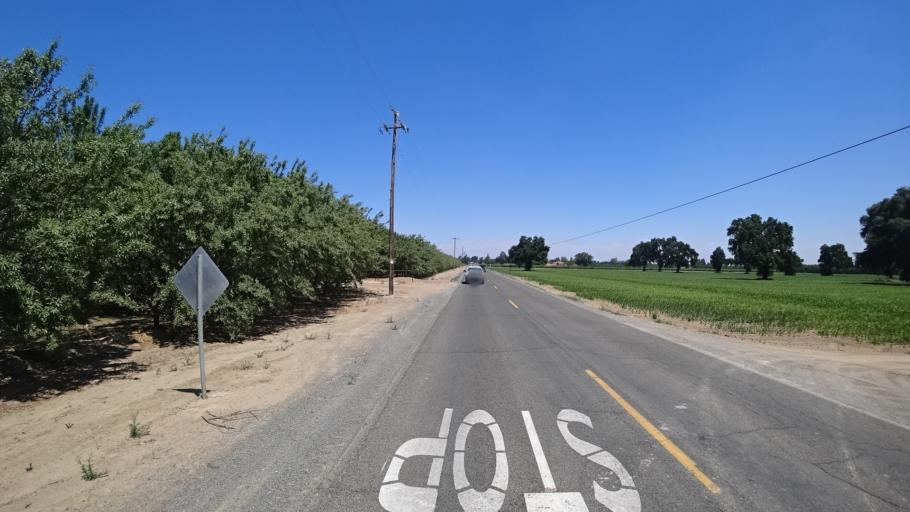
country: US
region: California
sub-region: Fresno County
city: Laton
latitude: 36.4231
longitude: -119.6842
